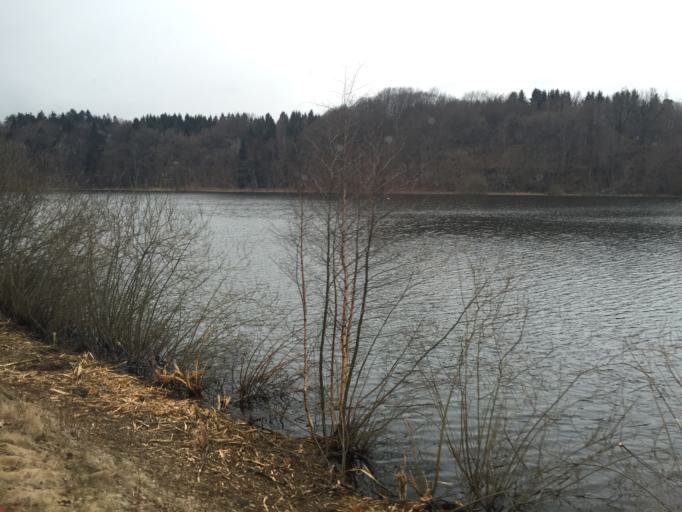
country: DK
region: Central Jutland
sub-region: Silkeborg Kommune
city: Virklund
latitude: 56.0285
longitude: 9.4870
